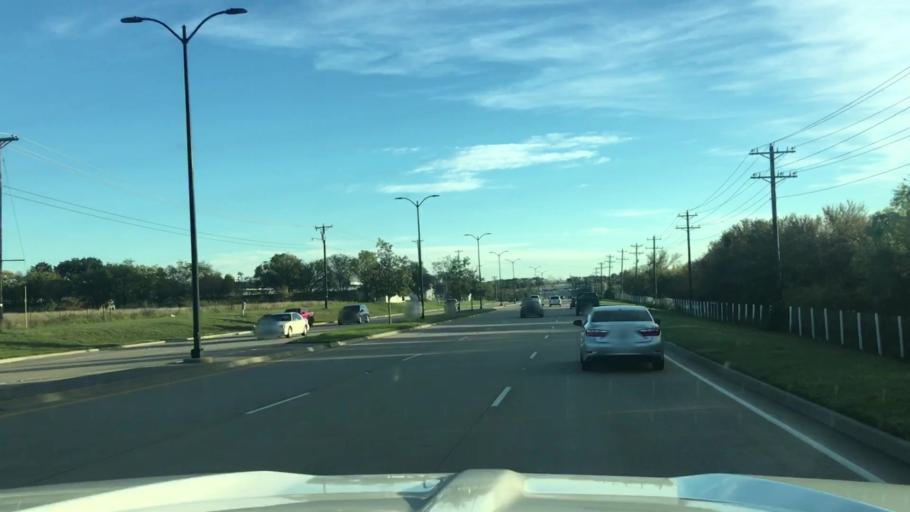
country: US
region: Texas
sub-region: Collin County
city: Frisco
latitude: 33.1845
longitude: -96.8031
